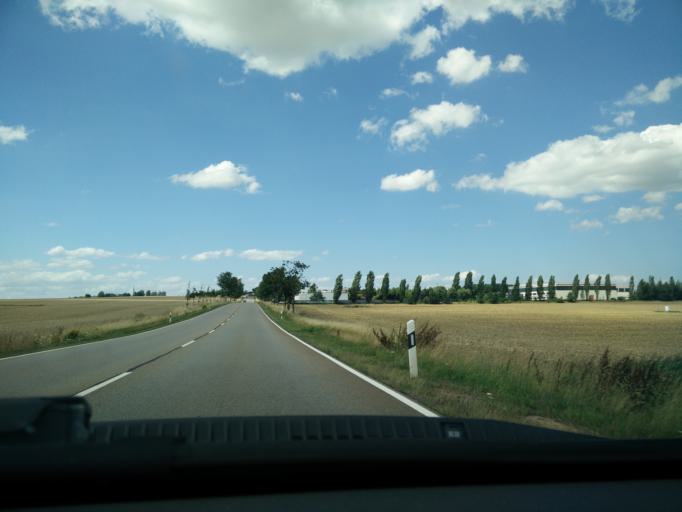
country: DE
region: Saxony
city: Hartmannsdorf
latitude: 50.8944
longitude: 12.7842
